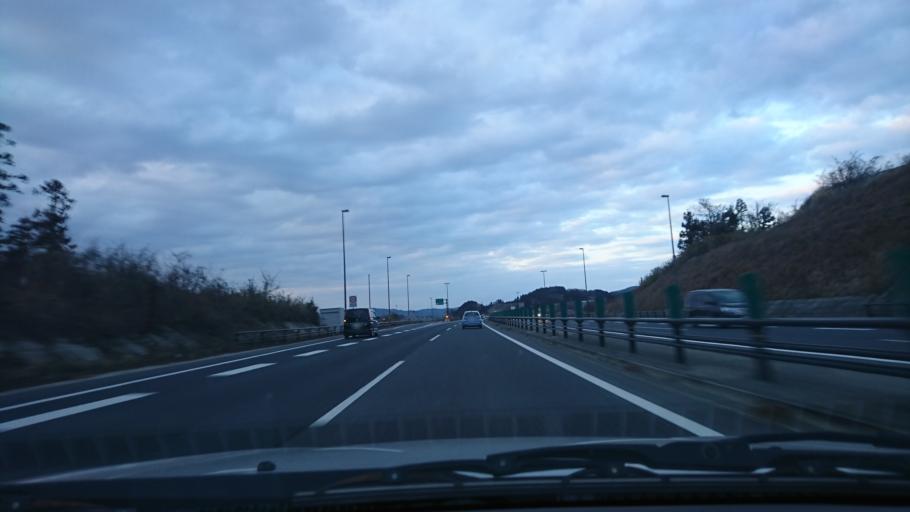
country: JP
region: Miyagi
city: Wakuya
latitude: 38.5589
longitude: 141.2704
